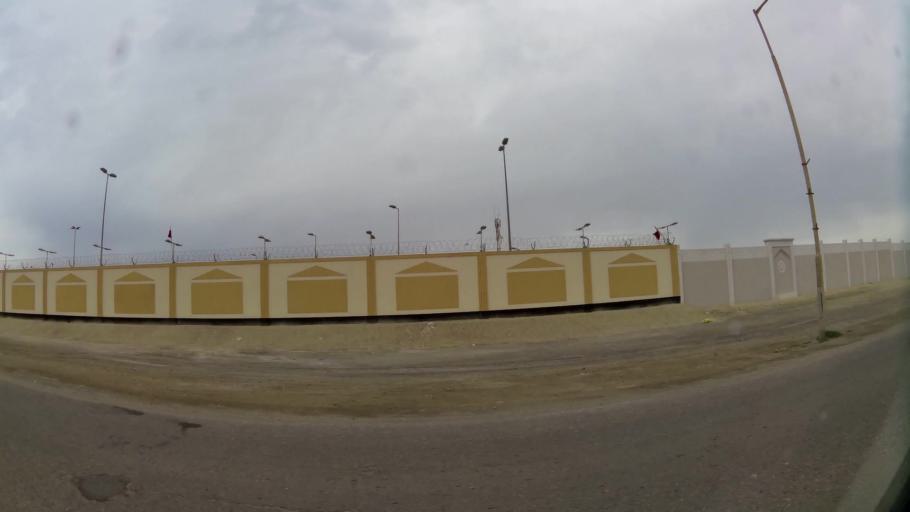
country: BH
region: Central Governorate
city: Madinat Hamad
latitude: 26.1310
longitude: 50.4793
